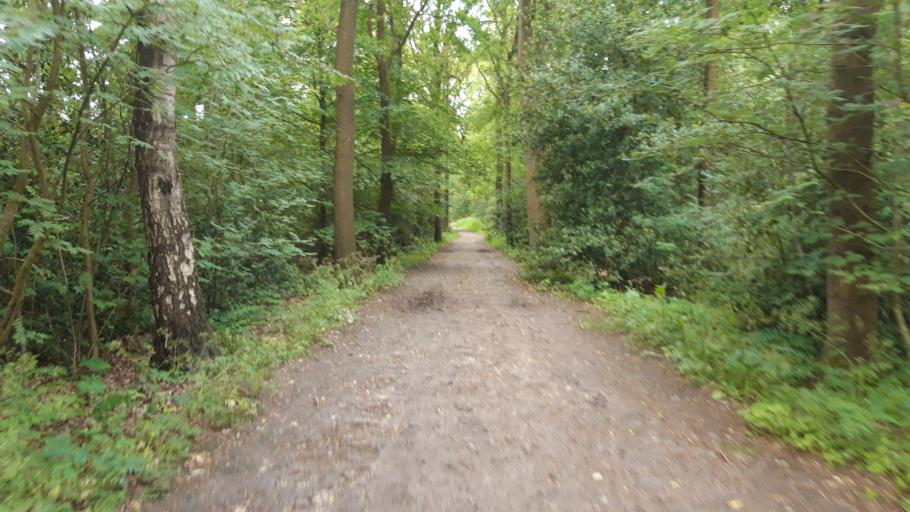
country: NL
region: Utrecht
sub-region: Gemeente Soest
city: Soest
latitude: 52.1568
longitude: 5.3202
